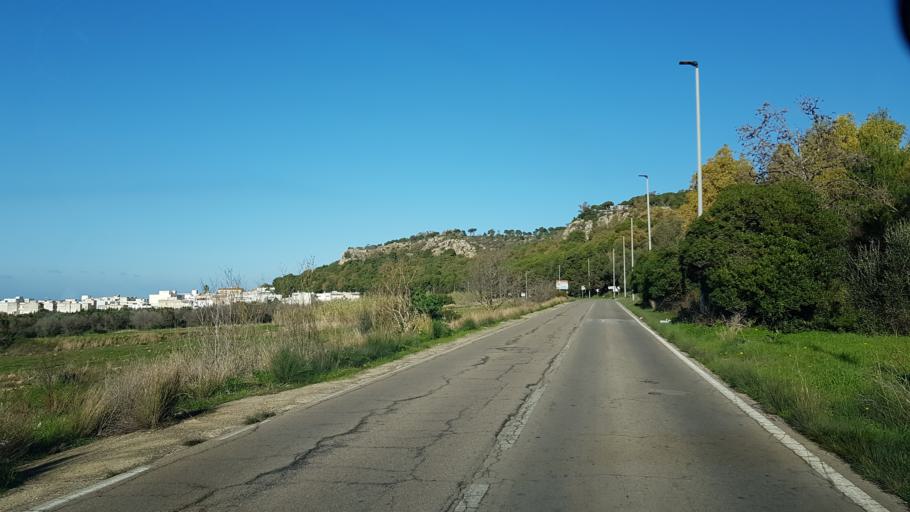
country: IT
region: Apulia
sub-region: Provincia di Lecce
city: Nardo
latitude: 40.1052
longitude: 18.0185
